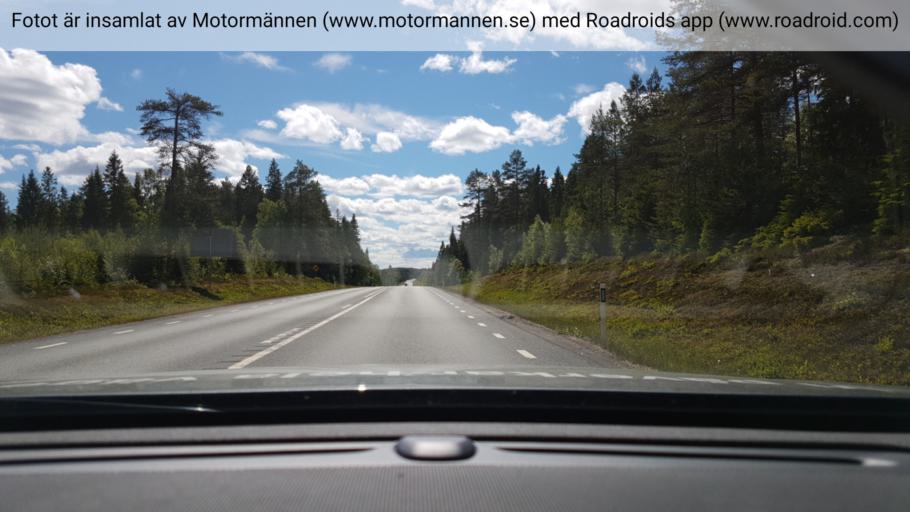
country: SE
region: Vaesterbotten
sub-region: Skelleftea Kommun
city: Burea
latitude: 64.3607
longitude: 21.2965
